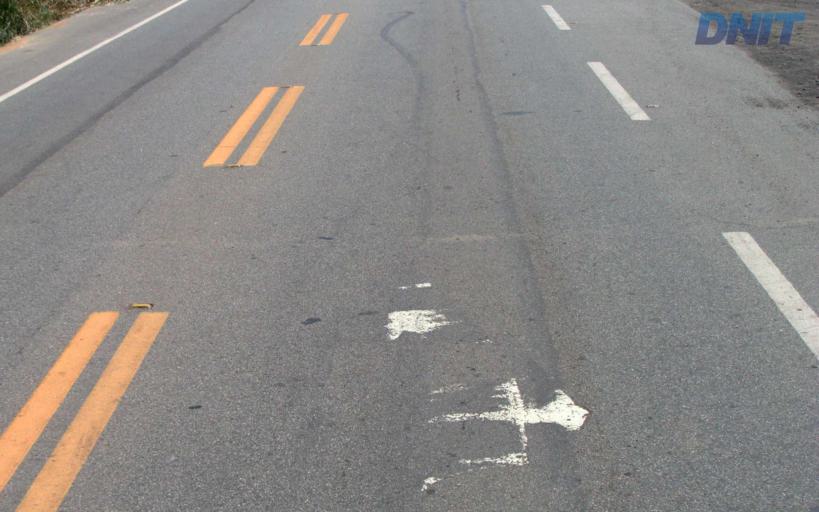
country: BR
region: Minas Gerais
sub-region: Timoteo
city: Timoteo
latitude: -19.5429
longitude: -42.6841
